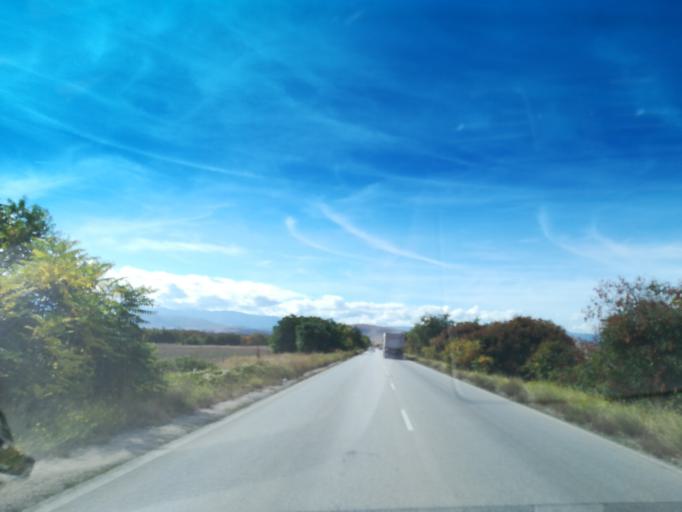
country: BG
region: Plovdiv
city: Stamboliyski
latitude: 42.1149
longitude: 24.5258
